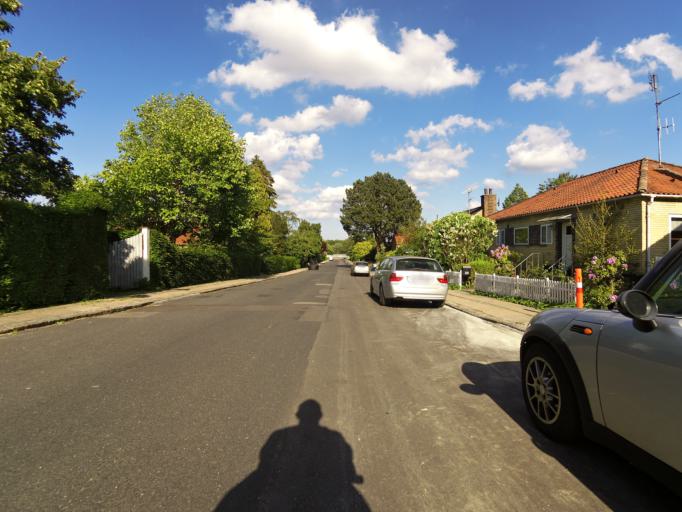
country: DK
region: Capital Region
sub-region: Lyngby-Tarbaek Kommune
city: Kongens Lyngby
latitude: 55.7448
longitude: 12.5284
